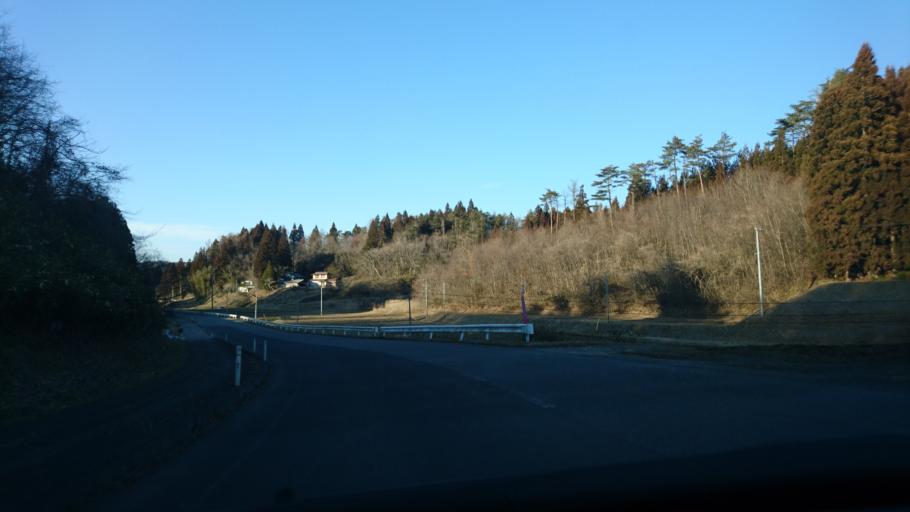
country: JP
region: Iwate
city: Ichinoseki
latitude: 38.9477
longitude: 141.3634
